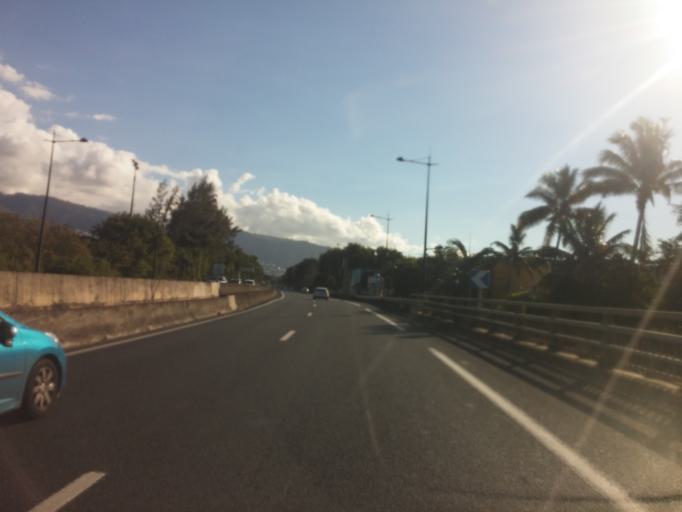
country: RE
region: Reunion
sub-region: Reunion
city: Saint-Denis
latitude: -20.8856
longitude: 55.4973
